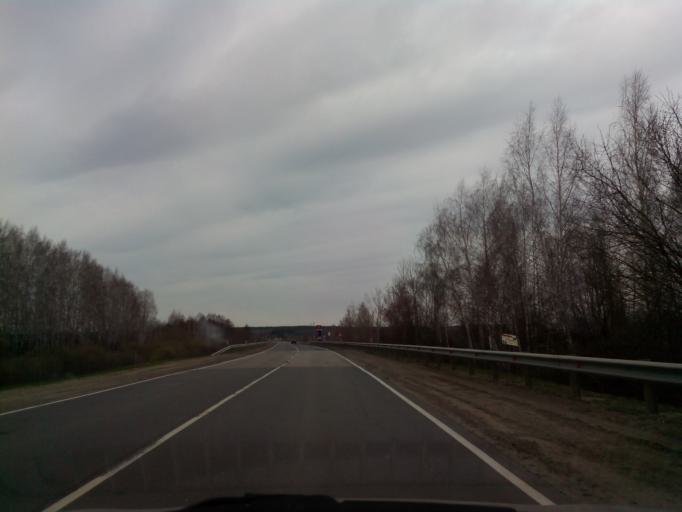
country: RU
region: Tambov
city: Znamenka
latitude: 52.5201
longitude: 41.3636
